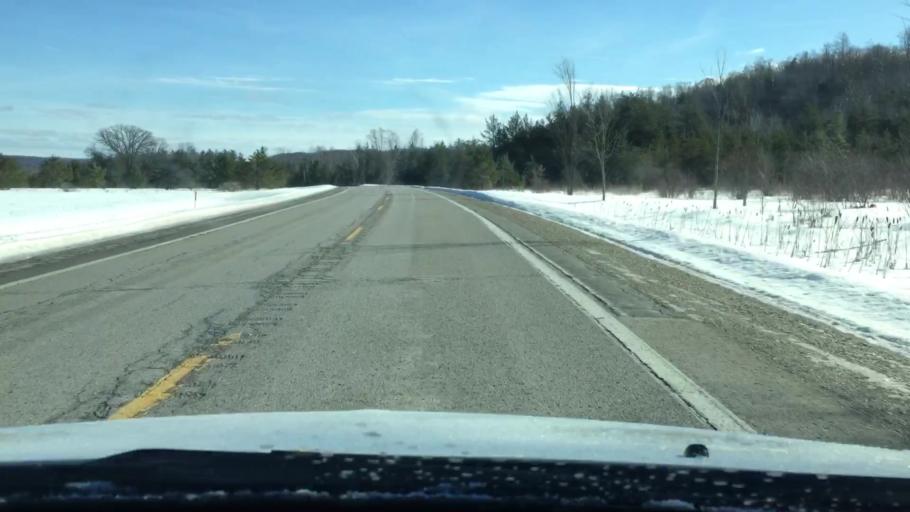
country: US
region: Michigan
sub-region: Charlevoix County
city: East Jordan
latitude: 45.1071
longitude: -85.1257
